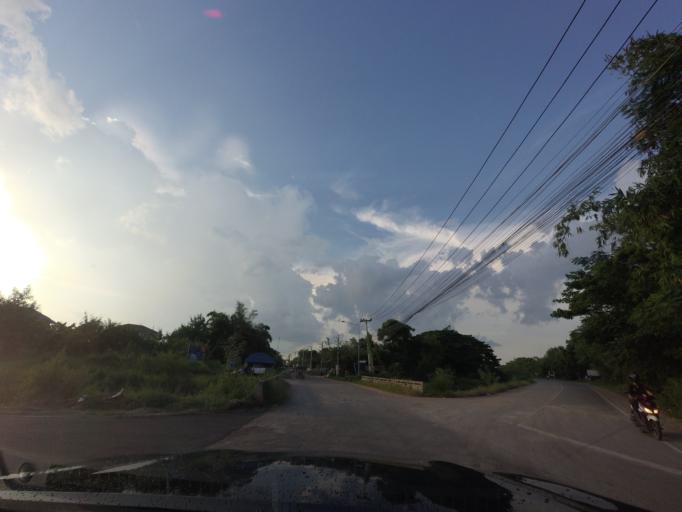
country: TH
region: Khon Kaen
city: Khon Kaen
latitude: 16.4036
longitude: 102.8645
